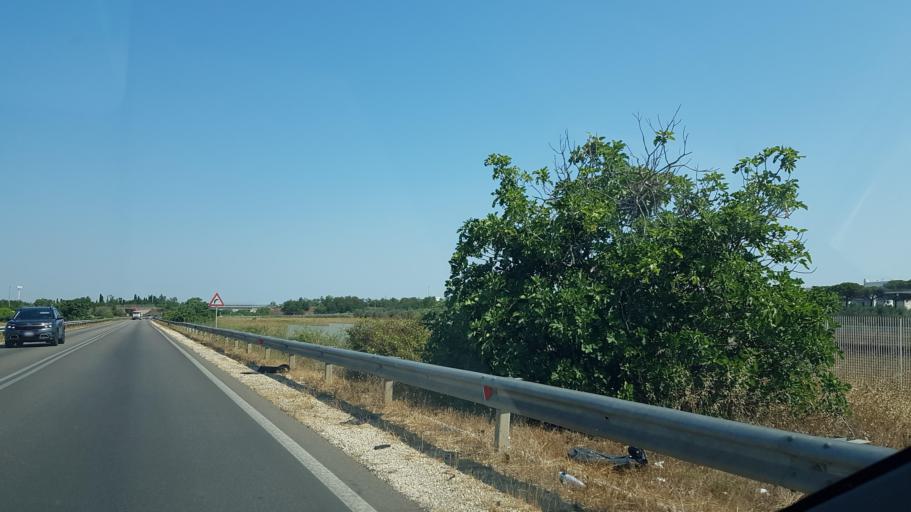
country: IT
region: Apulia
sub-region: Provincia di Lecce
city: Nociglia
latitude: 40.0344
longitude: 18.3228
